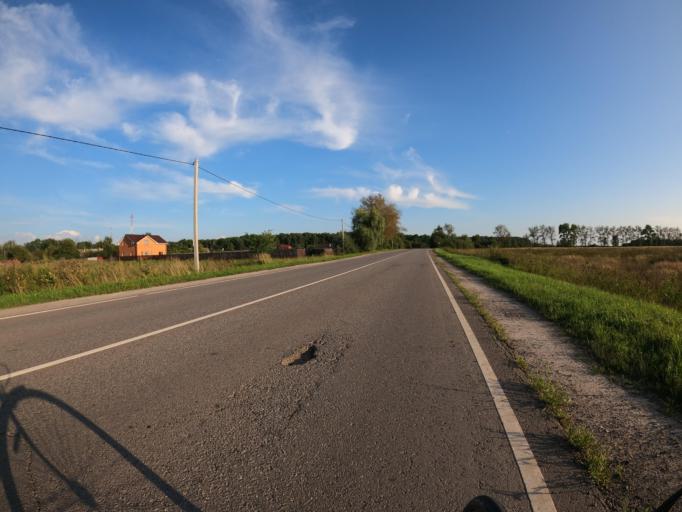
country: RU
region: Moskovskaya
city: Meshcherino
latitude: 55.1140
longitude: 38.3209
